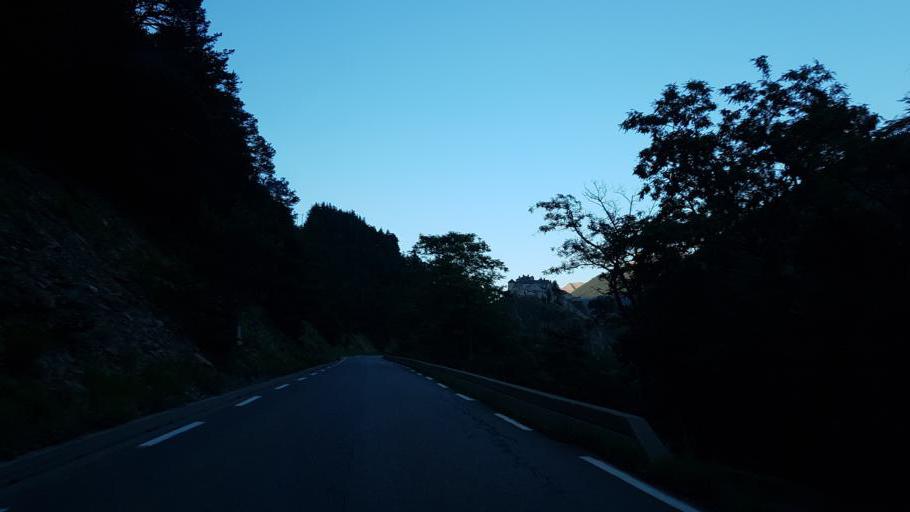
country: FR
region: Provence-Alpes-Cote d'Azur
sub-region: Departement des Hautes-Alpes
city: Guillestre
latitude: 44.7548
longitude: 6.7816
